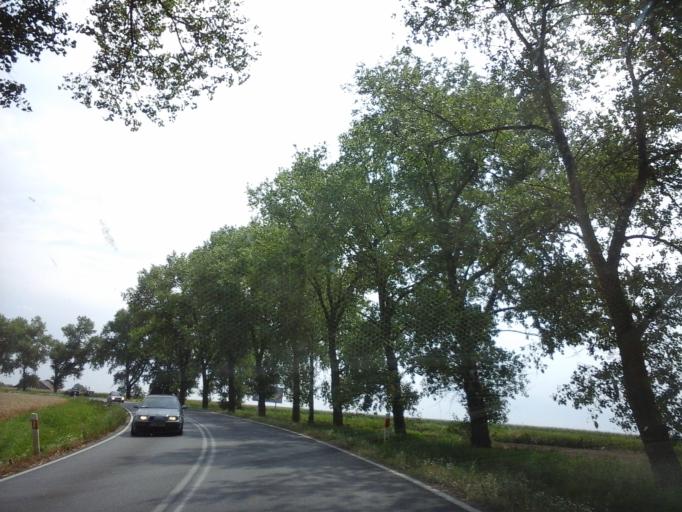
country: PL
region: Lower Silesian Voivodeship
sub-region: Powiat strzelinski
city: Strzelin
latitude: 50.8311
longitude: 17.0538
